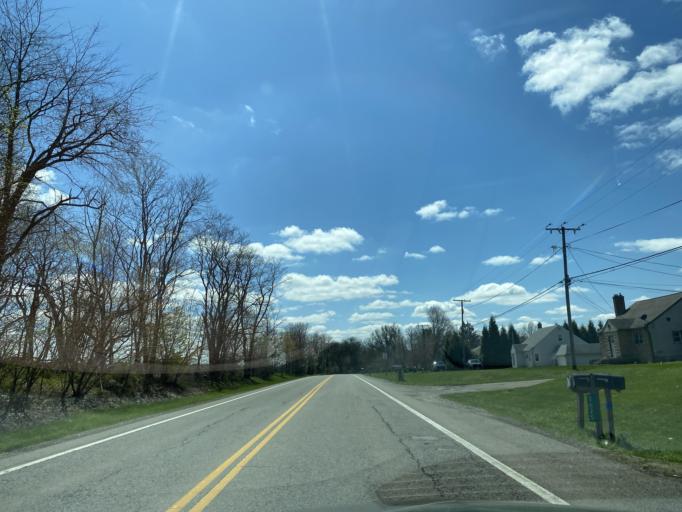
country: US
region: Ohio
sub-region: Wayne County
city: Wooster
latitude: 40.7671
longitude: -81.9728
